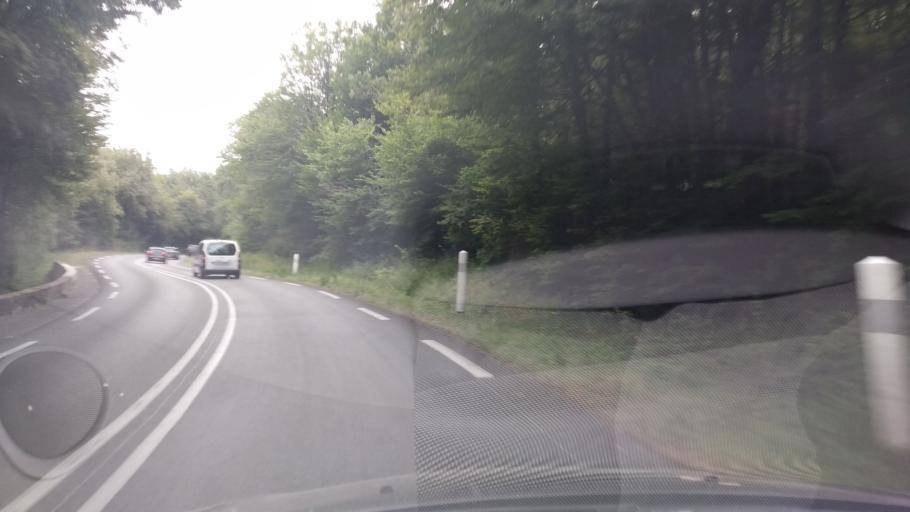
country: FR
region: Poitou-Charentes
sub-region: Departement de la Vienne
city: Saint-Benoit
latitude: 46.5466
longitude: 0.3520
